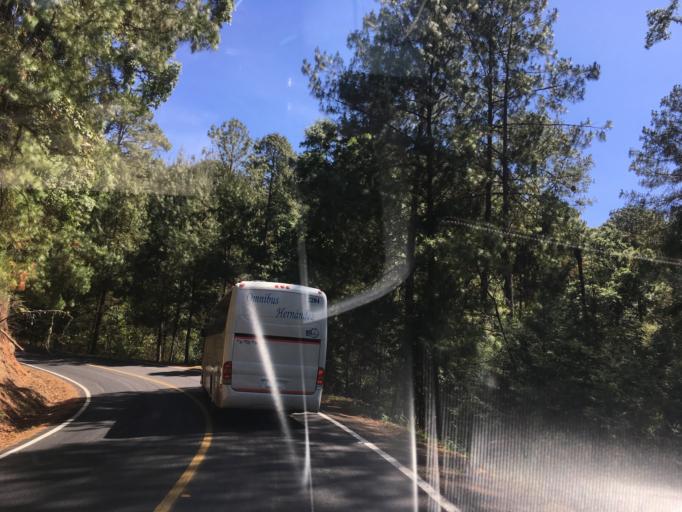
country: MX
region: Michoacan
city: Tzitzio
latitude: 19.6844
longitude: -100.8785
